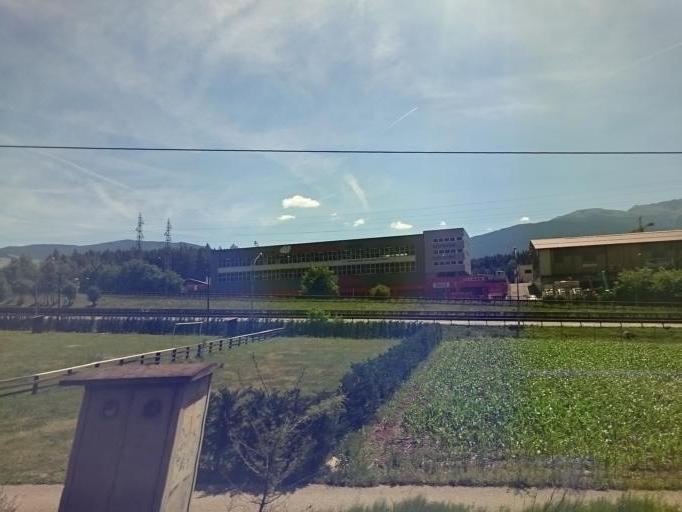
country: IT
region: Trentino-Alto Adige
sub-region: Bolzano
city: Varna
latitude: 46.7622
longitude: 11.6365
